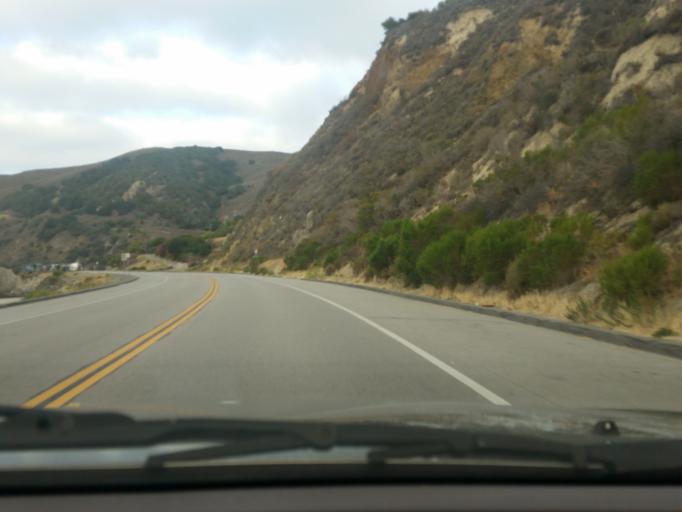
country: US
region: California
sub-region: San Luis Obispo County
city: Avila Beach
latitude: 35.1778
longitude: -120.7500
